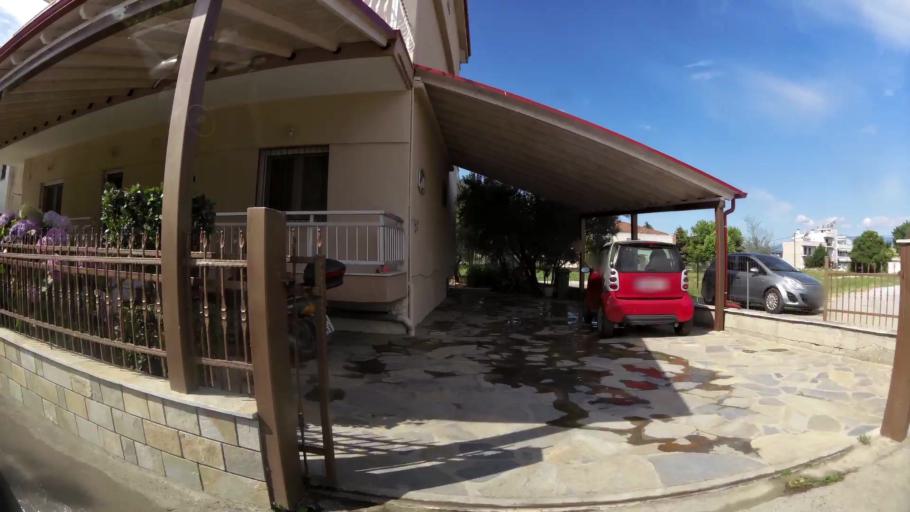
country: GR
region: Central Macedonia
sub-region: Nomos Pierias
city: Katerini
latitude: 40.2789
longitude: 22.5132
